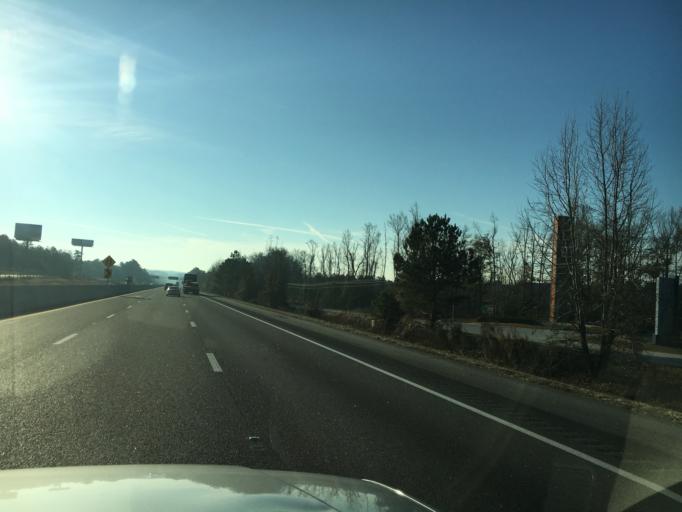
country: US
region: South Carolina
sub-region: Calhoun County
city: Oak Grove
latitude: 33.8050
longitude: -81.0032
